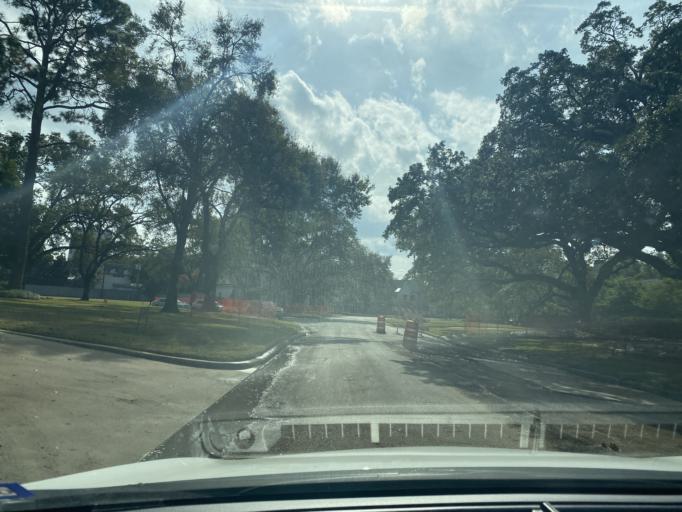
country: US
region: Texas
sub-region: Harris County
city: Hunters Creek Village
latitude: 29.7627
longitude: -95.4755
